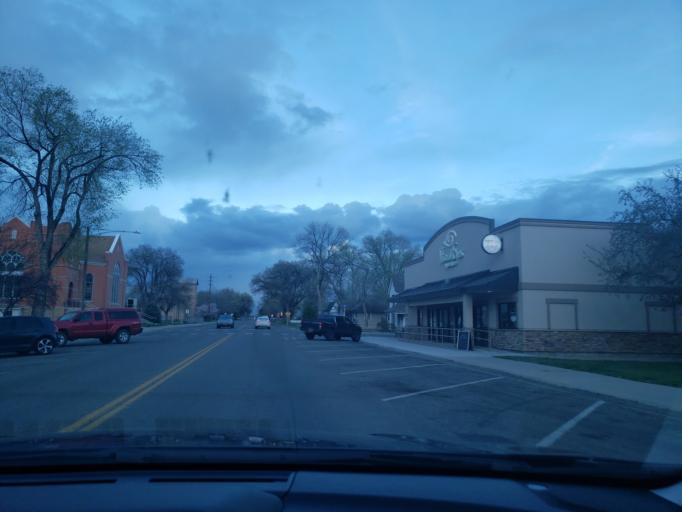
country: US
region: Colorado
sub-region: Mesa County
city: Fruita
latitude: 39.1589
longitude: -108.7309
